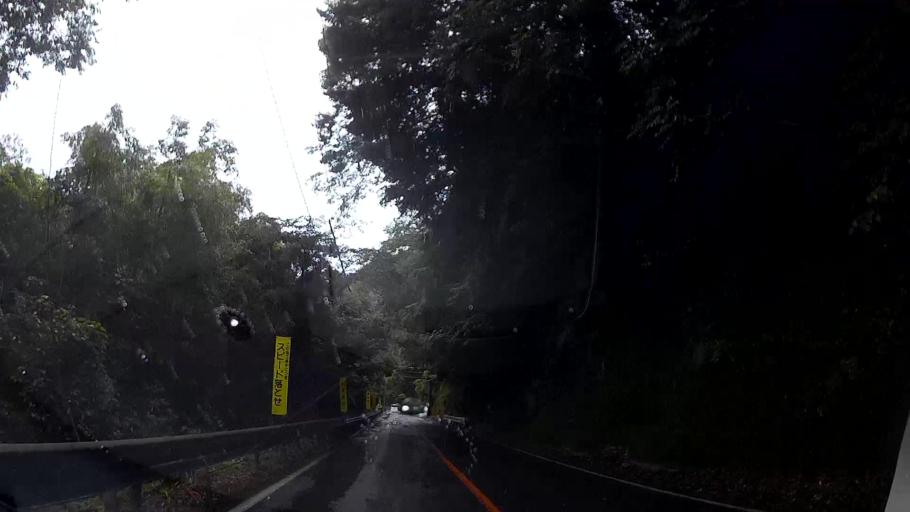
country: JP
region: Oita
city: Hita
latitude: 33.1803
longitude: 131.0049
